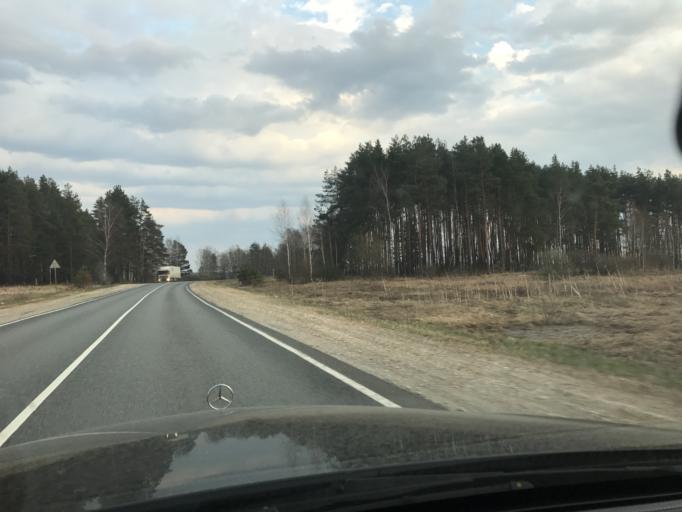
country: RU
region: Vladimir
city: Murom
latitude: 55.6340
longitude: 41.8735
